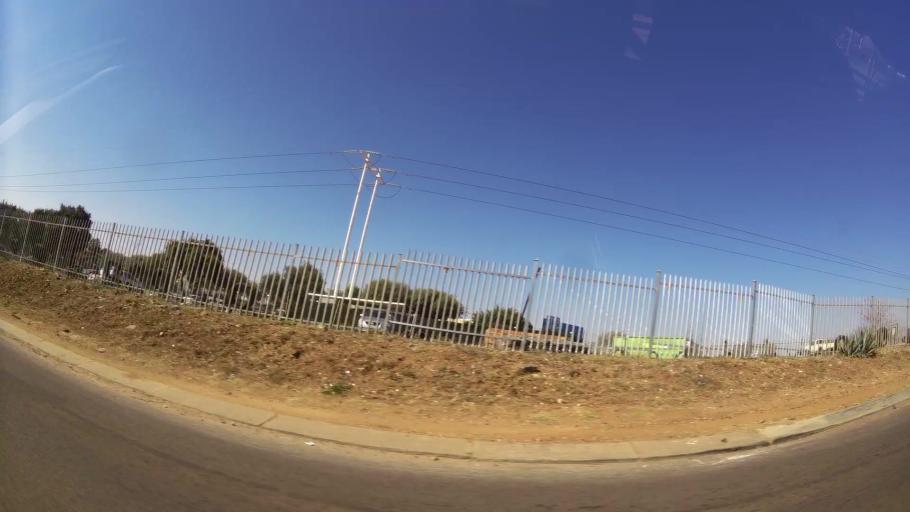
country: ZA
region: Gauteng
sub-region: City of Tshwane Metropolitan Municipality
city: Centurion
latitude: -25.8670
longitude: 28.1956
